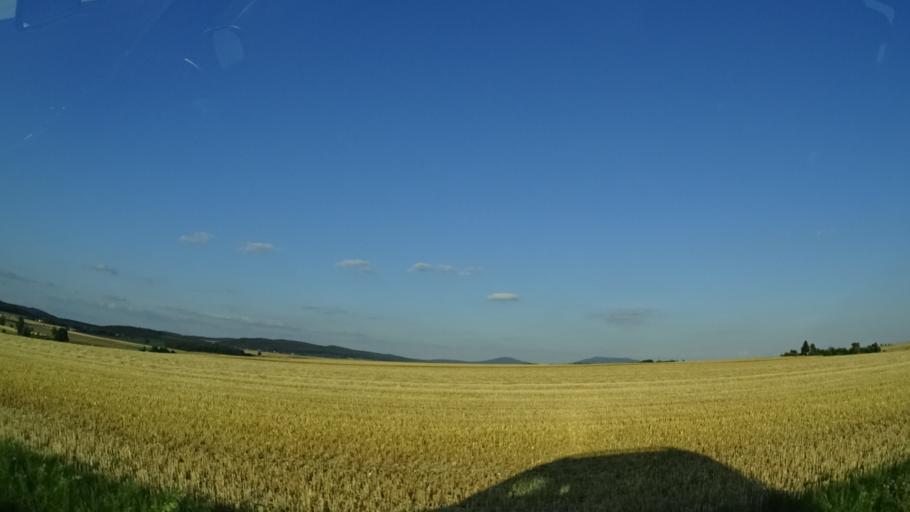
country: DE
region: Thuringia
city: Wolfershausen
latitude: 50.4444
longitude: 10.4005
